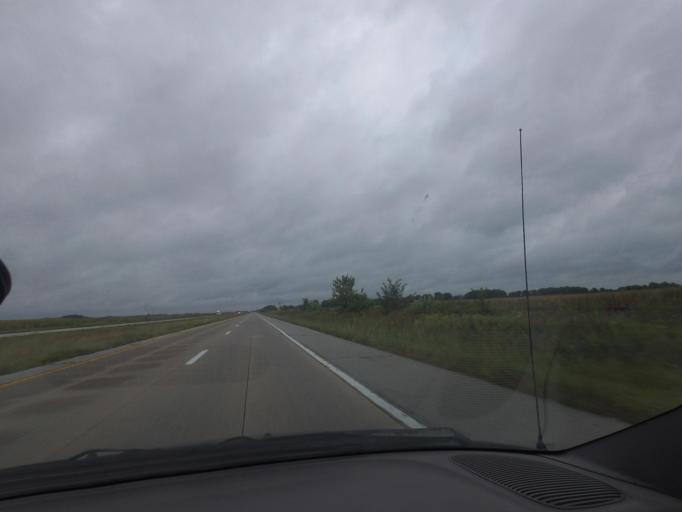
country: US
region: Missouri
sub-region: Marion County
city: Monroe City
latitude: 39.6641
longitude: -91.8446
